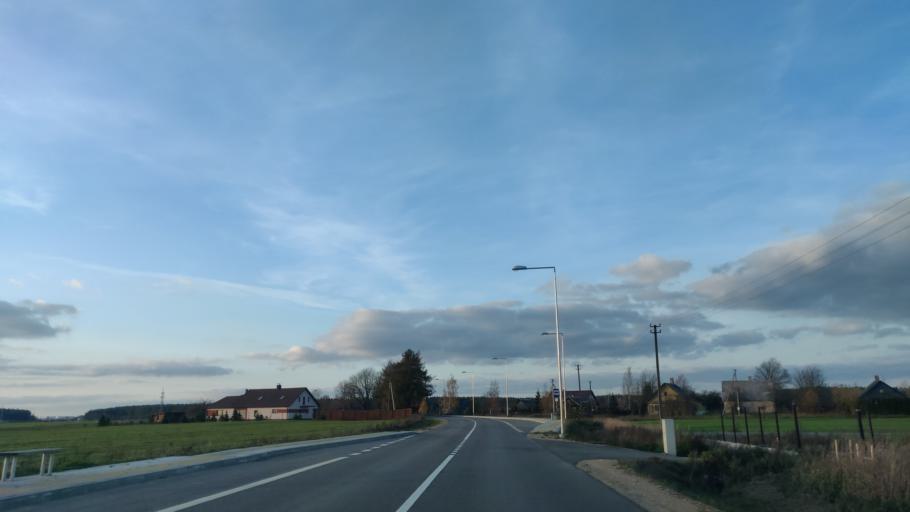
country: LT
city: Lentvaris
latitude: 54.5904
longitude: 25.0491
